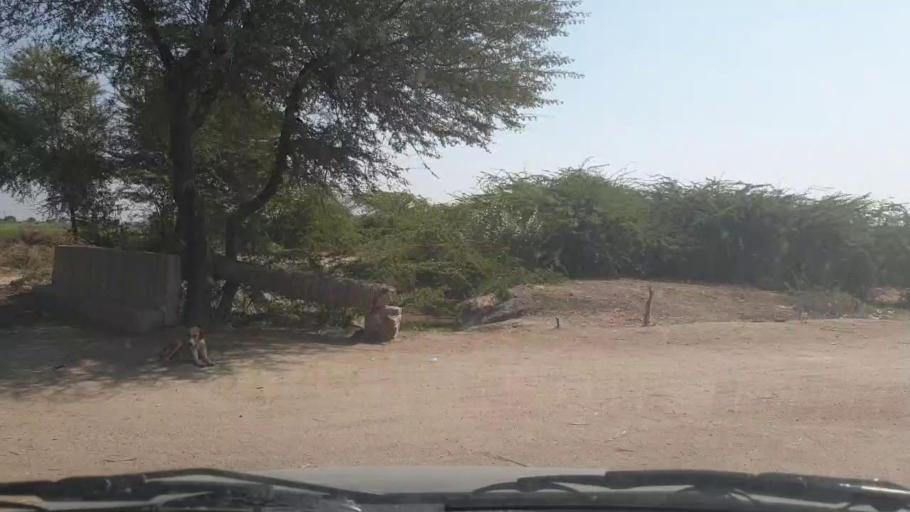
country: PK
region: Sindh
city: Samaro
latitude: 25.2262
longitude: 69.3226
